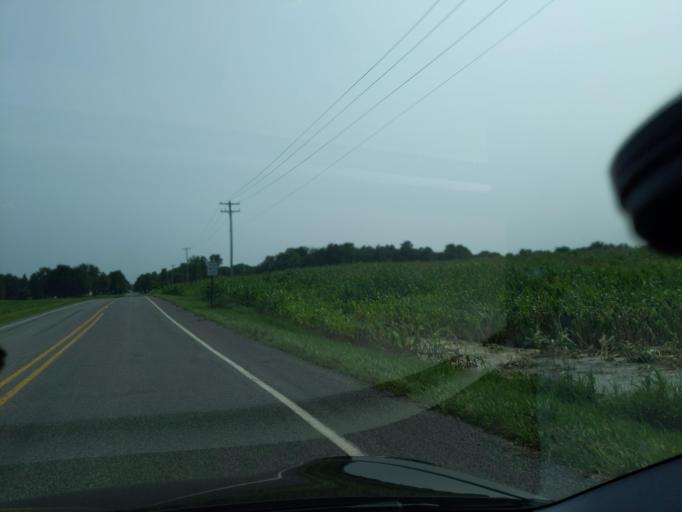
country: US
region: Michigan
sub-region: Ingham County
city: Holt
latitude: 42.5868
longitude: -84.5625
